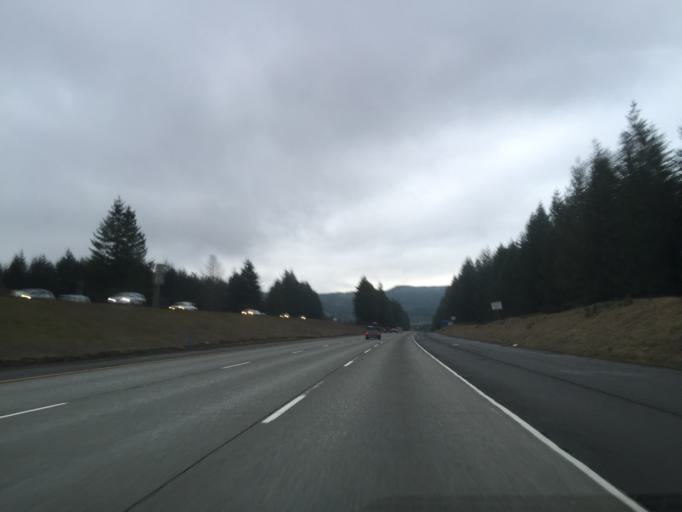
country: US
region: Washington
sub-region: King County
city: Tanner
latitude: 47.4701
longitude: -121.7310
